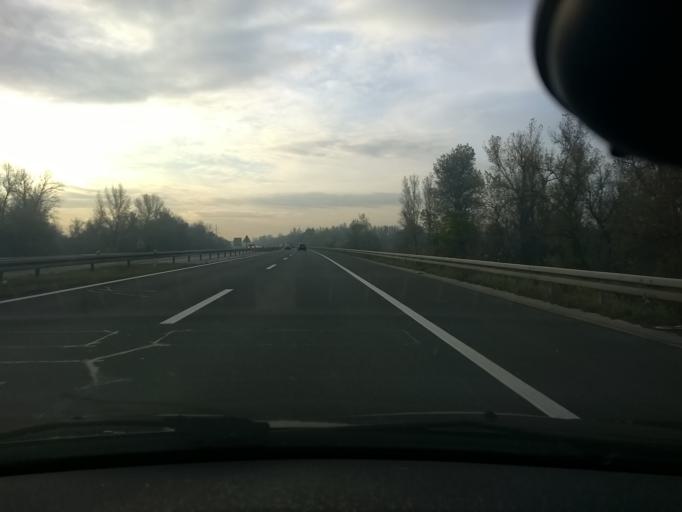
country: HR
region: Zagrebacka
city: Bestovje
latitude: 45.8233
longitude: 15.8207
